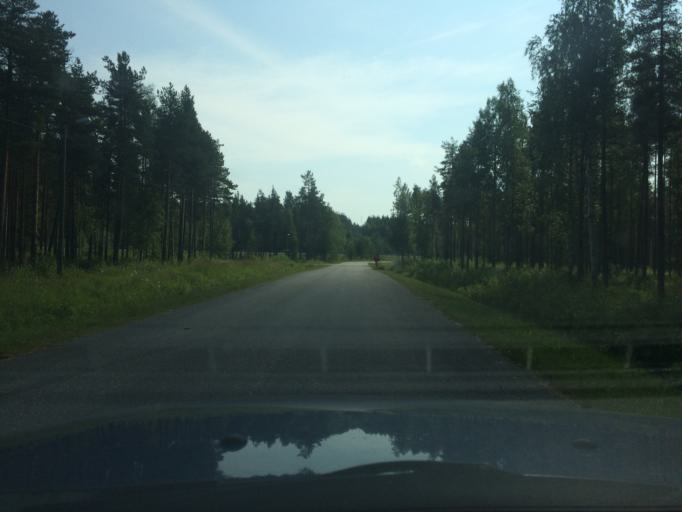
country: SE
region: Norrbotten
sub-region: Pitea Kommun
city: Pitea
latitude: 65.3416
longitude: 21.4351
